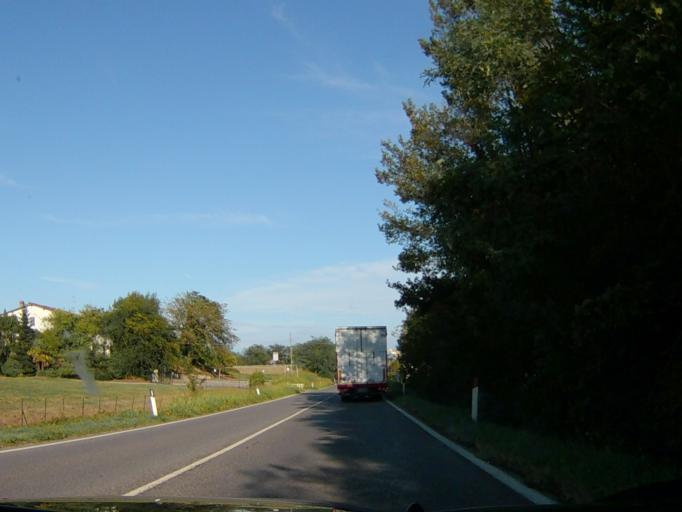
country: IT
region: Lombardy
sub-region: Provincia di Brescia
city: Lonato
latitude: 45.4623
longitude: 10.5042
